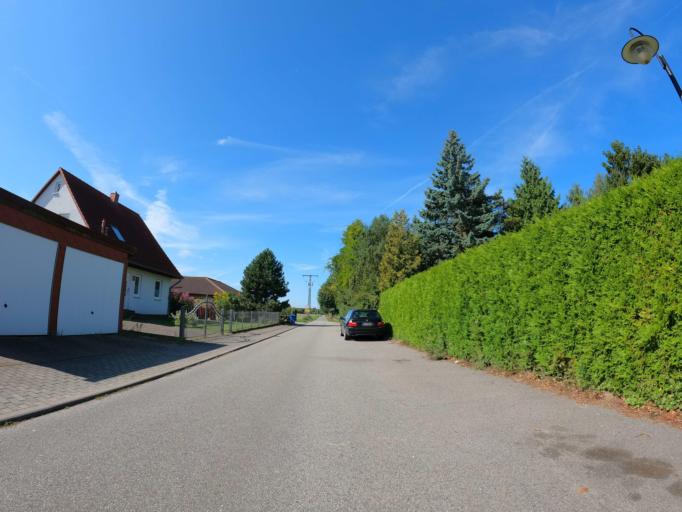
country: DE
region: Mecklenburg-Vorpommern
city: Kramerhof
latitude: 54.3512
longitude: 13.0645
